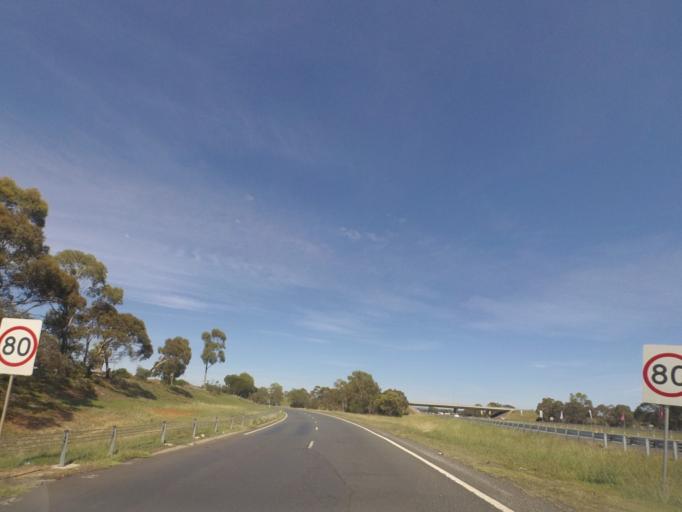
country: AU
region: Victoria
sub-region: Melton
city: Melton West
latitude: -37.6910
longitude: 144.5703
